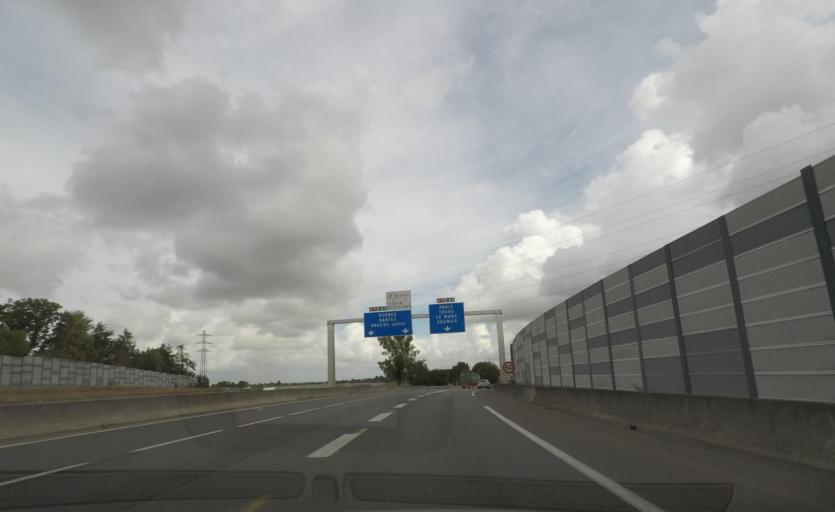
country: FR
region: Pays de la Loire
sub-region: Departement de Maine-et-Loire
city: Ecouflant
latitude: 47.4993
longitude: -0.5010
